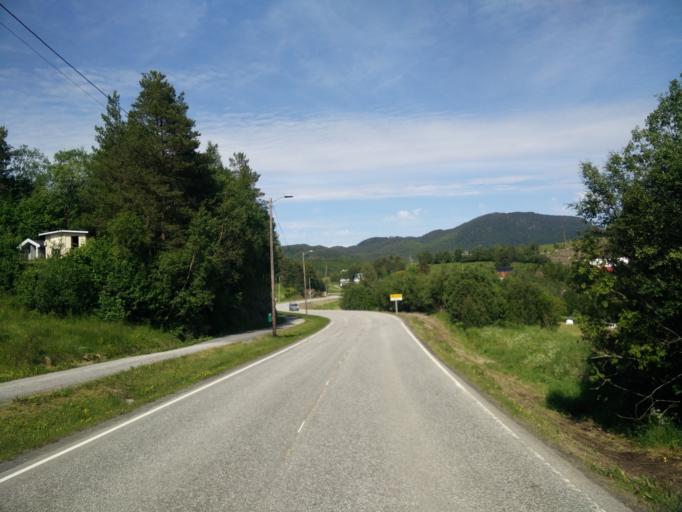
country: NO
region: More og Romsdal
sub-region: Tingvoll
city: Tingvoll
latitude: 63.0368
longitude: 8.0423
